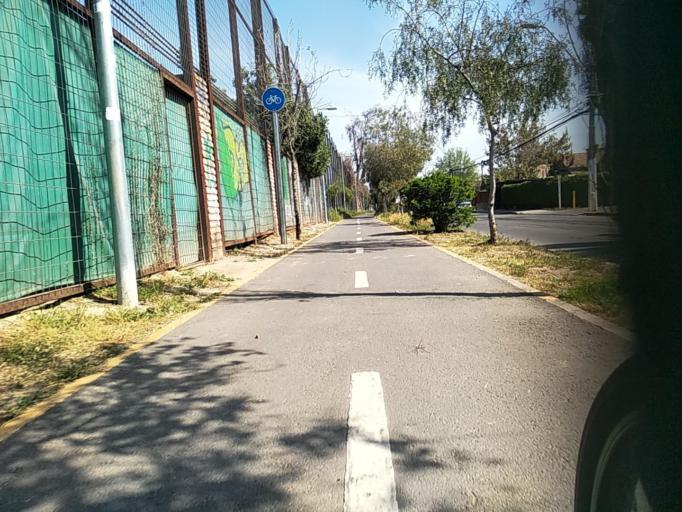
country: CL
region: Santiago Metropolitan
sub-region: Provincia de Santiago
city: Villa Presidente Frei, Nunoa, Santiago, Chile
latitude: -33.5033
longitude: -70.6064
